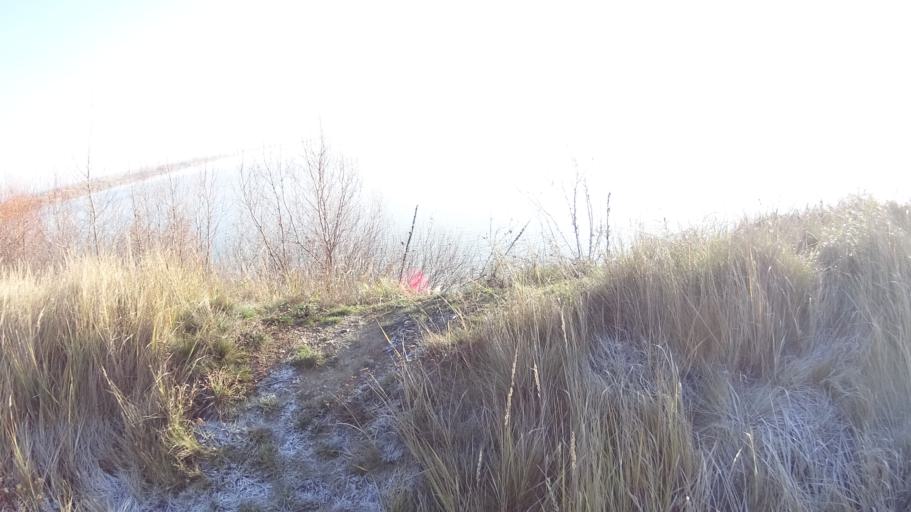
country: HU
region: Borsod-Abauj-Zemplen
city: Onod
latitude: 47.9954
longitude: 20.8812
